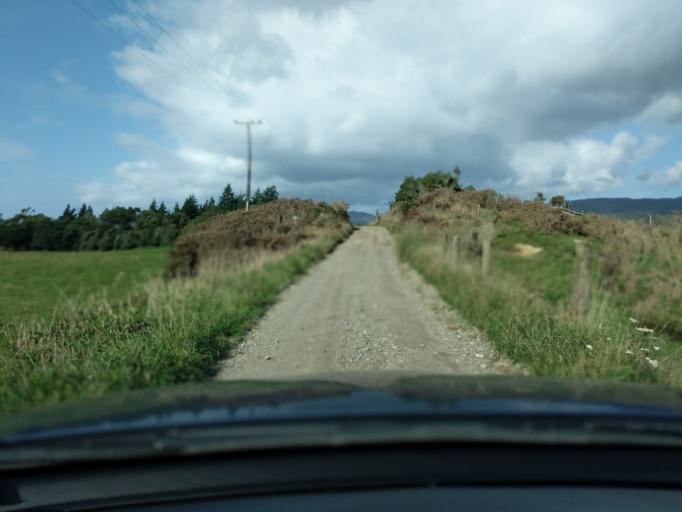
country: NZ
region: Tasman
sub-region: Tasman District
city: Takaka
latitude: -40.6523
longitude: 172.4692
